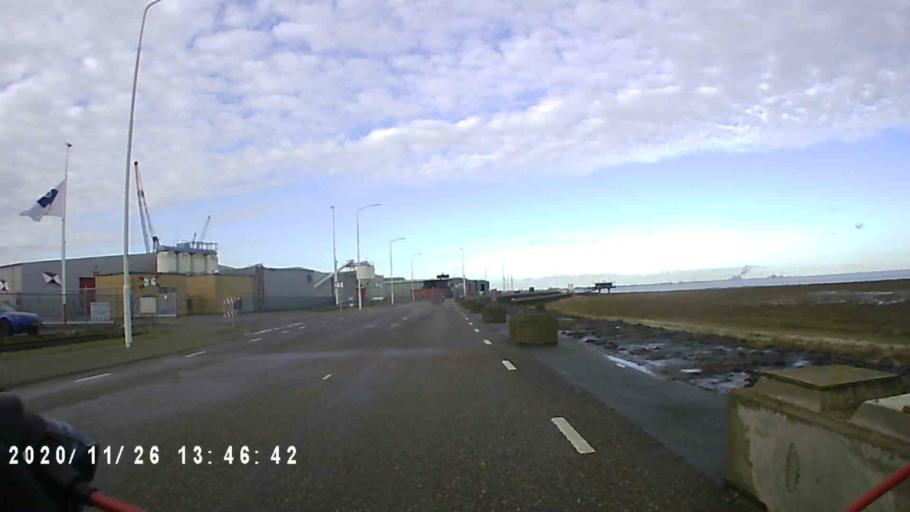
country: NL
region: Groningen
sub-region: Gemeente Delfzijl
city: Delfzijl
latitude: 53.3318
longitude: 6.9392
